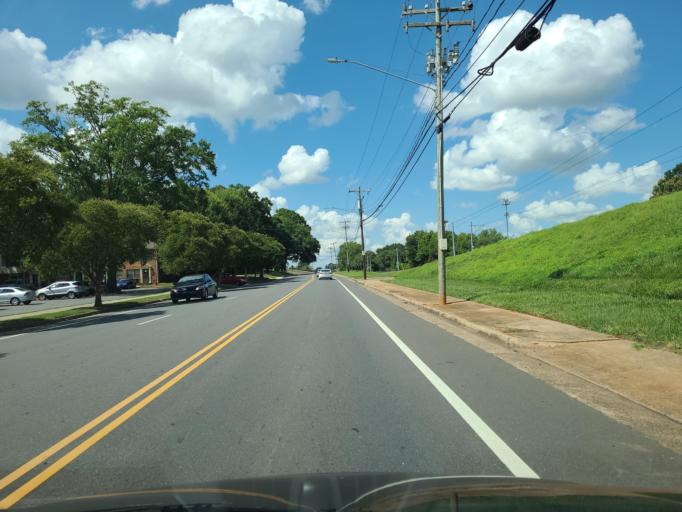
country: US
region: North Carolina
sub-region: Mecklenburg County
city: Pineville
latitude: 35.1540
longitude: -80.8776
